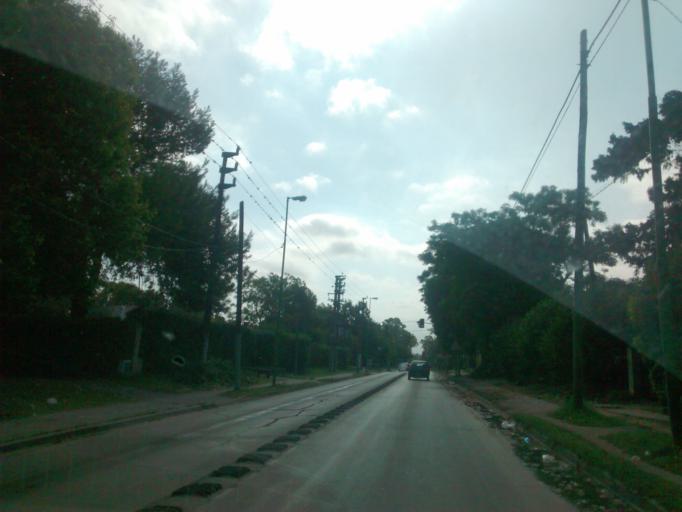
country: AR
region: Buenos Aires
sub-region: Partido de La Plata
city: La Plata
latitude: -34.9524
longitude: -57.9002
